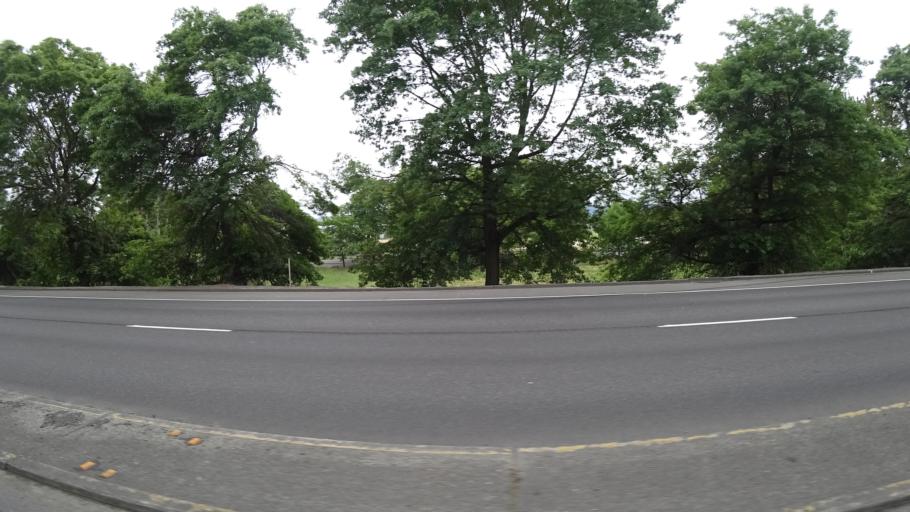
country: US
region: Washington
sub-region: Clark County
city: Vancouver
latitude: 45.5992
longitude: -122.6745
